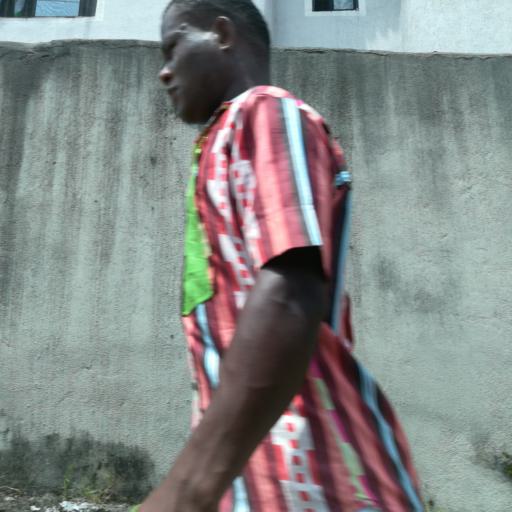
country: NG
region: Rivers
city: Port Harcourt
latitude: 4.7765
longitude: 7.0439
